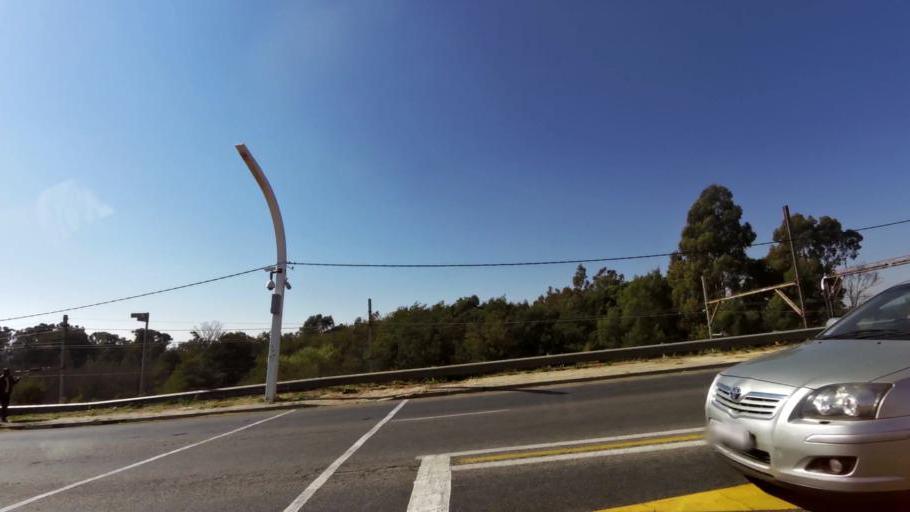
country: ZA
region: Gauteng
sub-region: City of Johannesburg Metropolitan Municipality
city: Johannesburg
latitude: -26.2368
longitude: 27.9854
